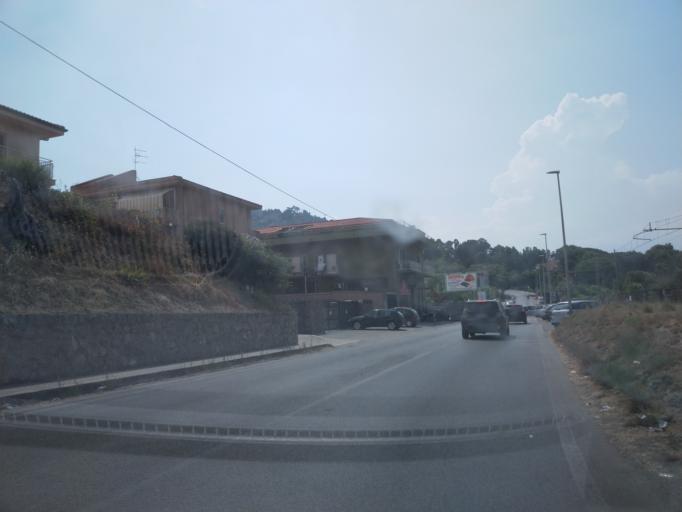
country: IT
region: Sicily
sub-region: Palermo
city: Cefalu
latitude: 38.0317
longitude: 14.0102
